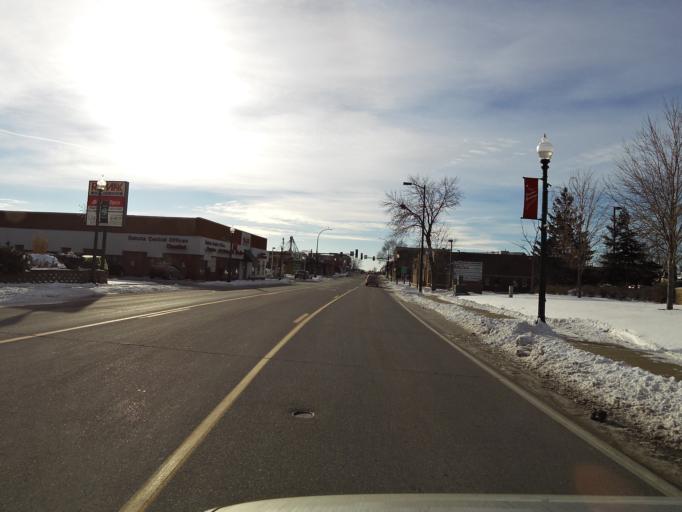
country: US
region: Minnesota
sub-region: Dakota County
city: Rosemount
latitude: 44.7404
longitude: -93.1261
